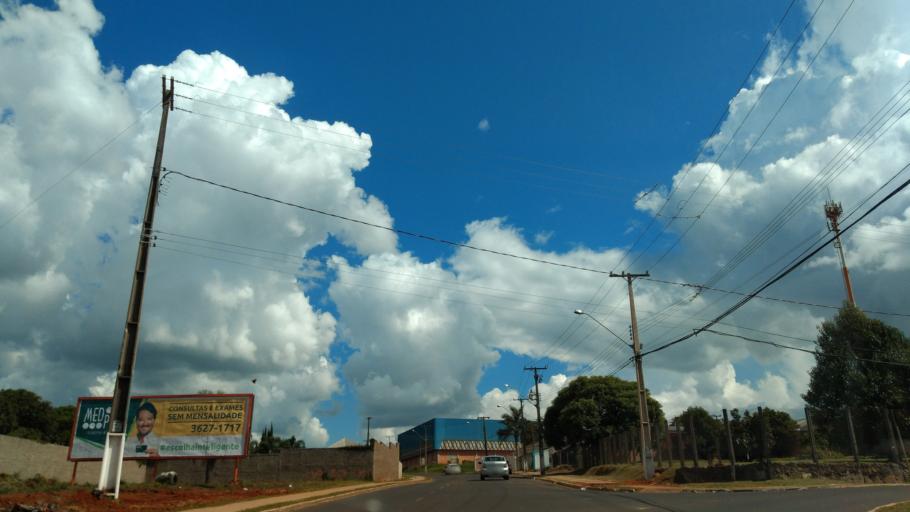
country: BR
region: Parana
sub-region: Guarapuava
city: Guarapuava
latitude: -25.3973
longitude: -51.4935
